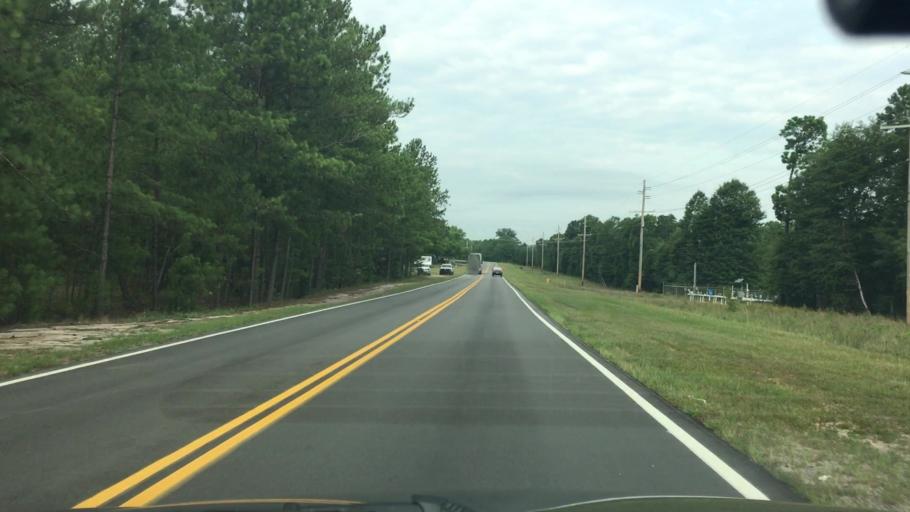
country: US
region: South Carolina
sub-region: Aiken County
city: Aiken
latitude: 33.6536
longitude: -81.6943
